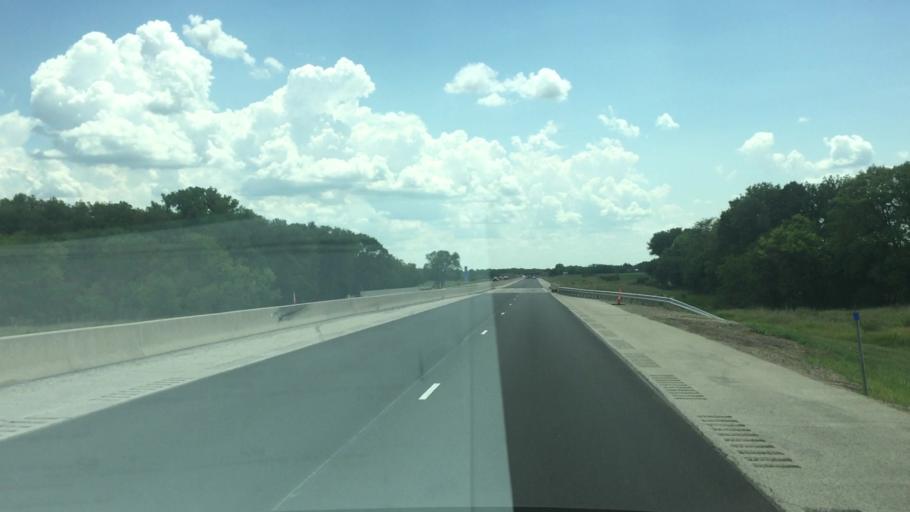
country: US
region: Kansas
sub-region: Lyon County
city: Emporia
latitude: 38.5195
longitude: -96.1431
